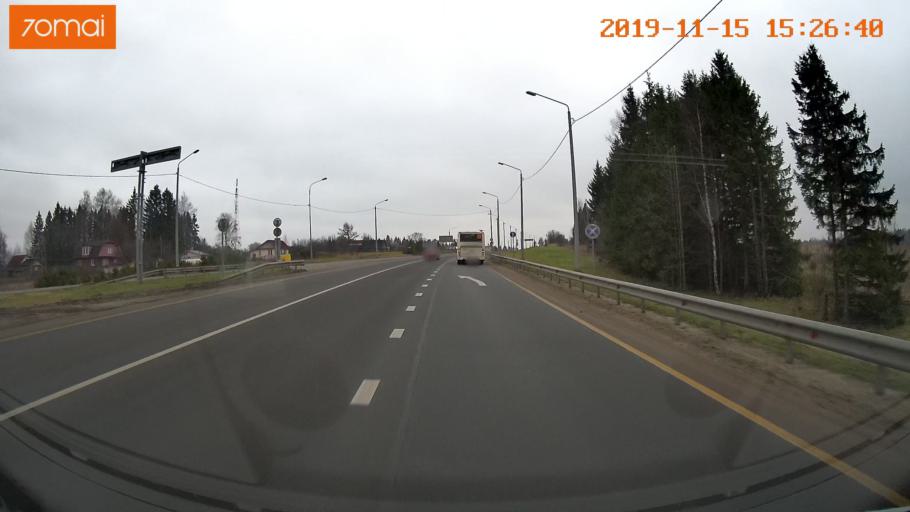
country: RU
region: Jaroslavl
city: Danilov
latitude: 58.1489
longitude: 40.1482
